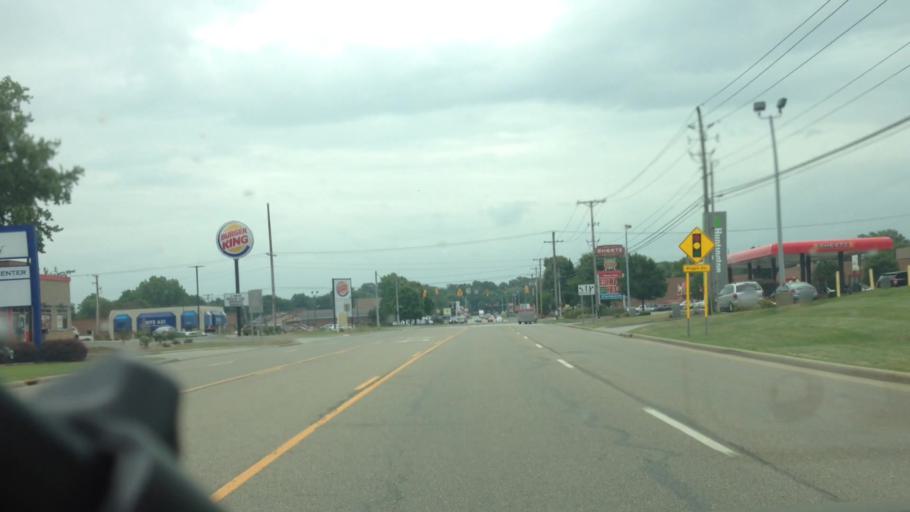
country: US
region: Ohio
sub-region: Stark County
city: North Canton
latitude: 40.8330
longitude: -81.4261
